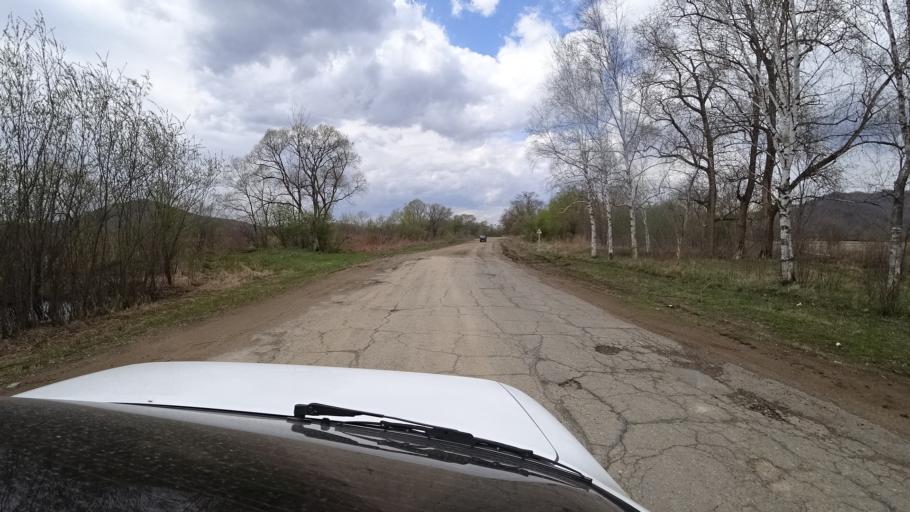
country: RU
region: Primorskiy
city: Novopokrovka
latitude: 45.6097
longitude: 134.2760
